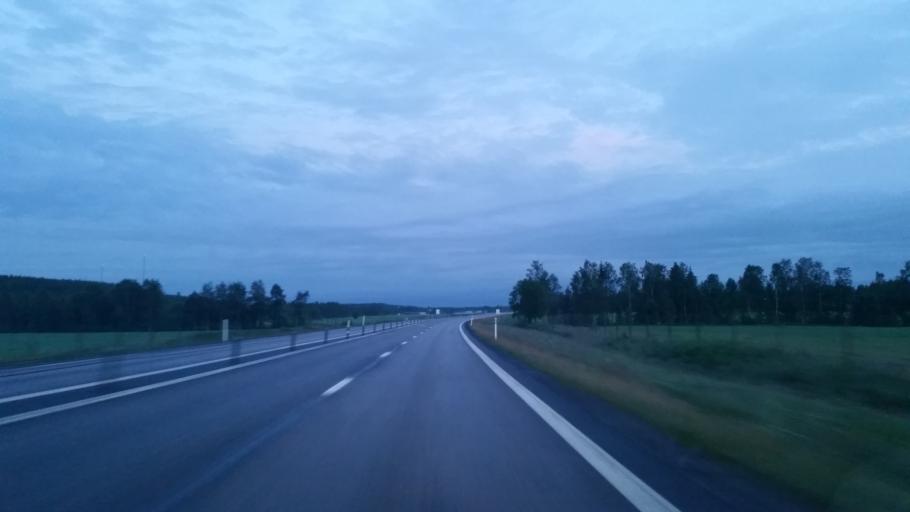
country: SE
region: Vaesterbotten
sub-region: Robertsfors Kommun
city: Robertsfors
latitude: 64.0836
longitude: 20.8677
